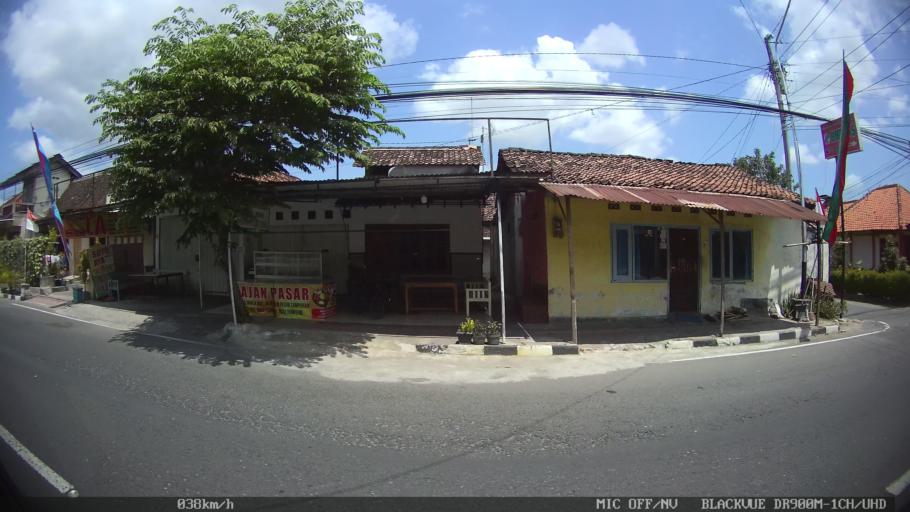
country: ID
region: Daerah Istimewa Yogyakarta
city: Bantul
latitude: -7.8923
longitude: 110.3313
